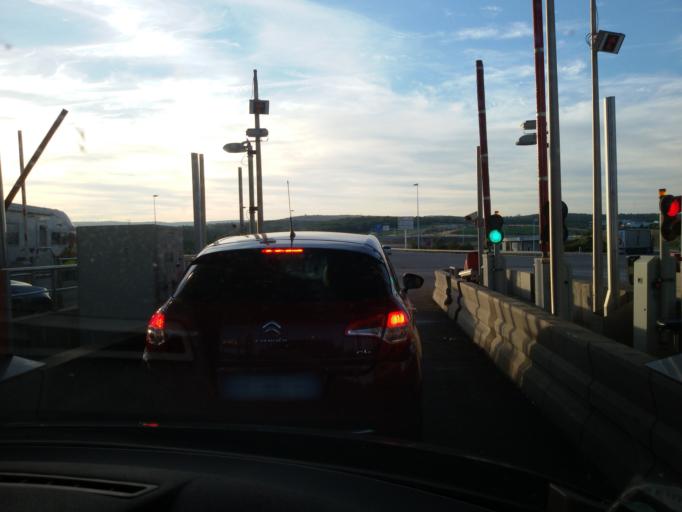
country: FR
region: Midi-Pyrenees
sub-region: Departement de l'Aveyron
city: Creissels
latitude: 44.1342
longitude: 3.0257
